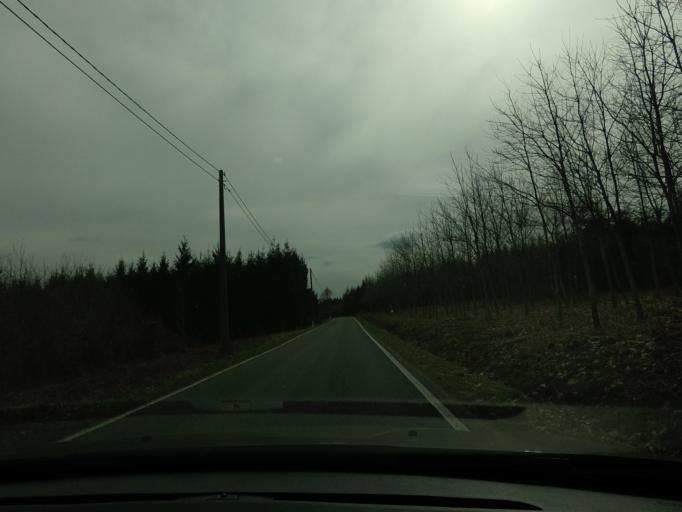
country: BE
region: Wallonia
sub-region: Province de Liege
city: Aywaille
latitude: 50.4182
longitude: 5.7152
